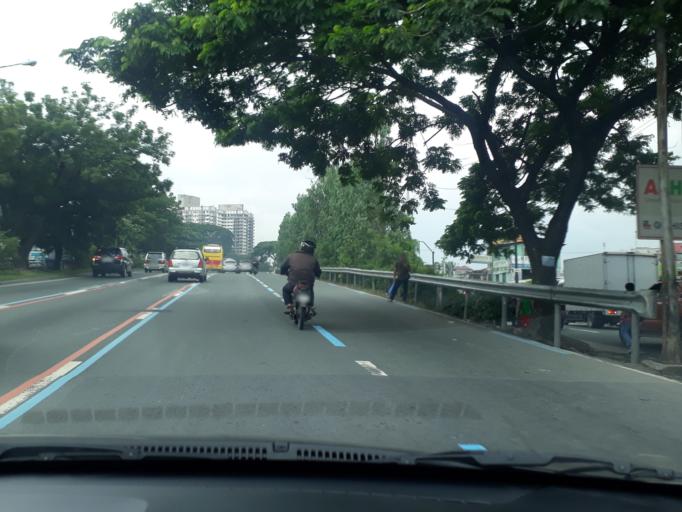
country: PH
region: Calabarzon
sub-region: Province of Rizal
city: Pateros
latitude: 14.5341
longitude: 121.0576
